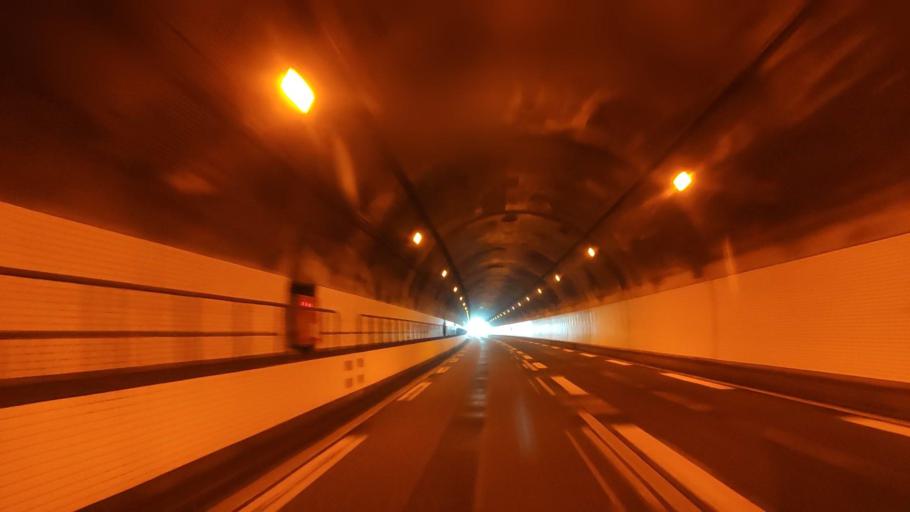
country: JP
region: Niigata
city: Itoigawa
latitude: 37.0210
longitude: 137.8402
